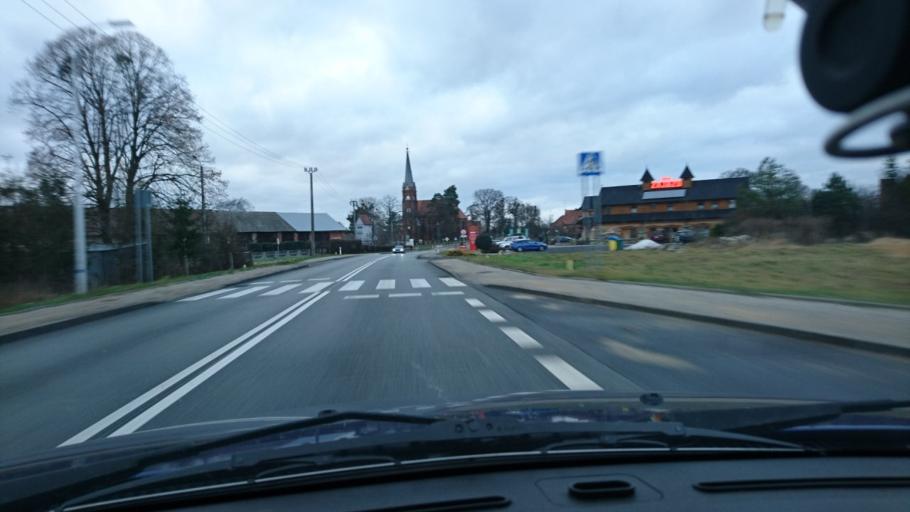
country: PL
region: Opole Voivodeship
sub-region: Powiat kluczborski
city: Kluczbork
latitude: 51.0263
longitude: 18.1923
